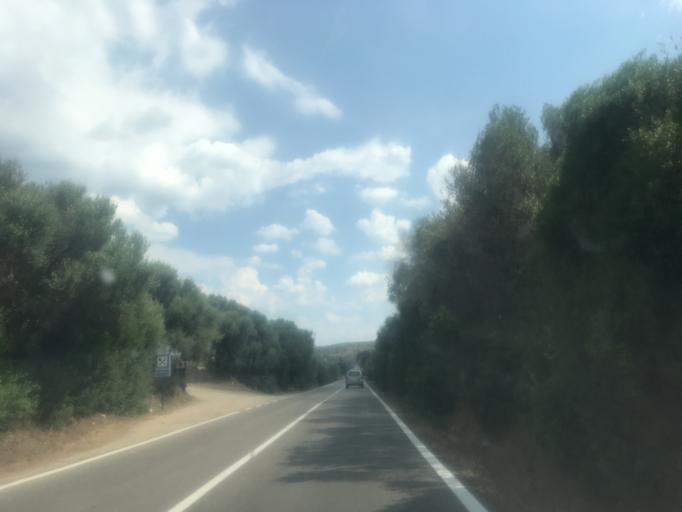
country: IT
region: Sardinia
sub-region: Provincia di Olbia-Tempio
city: San Teodoro
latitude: 40.8517
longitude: 9.6462
